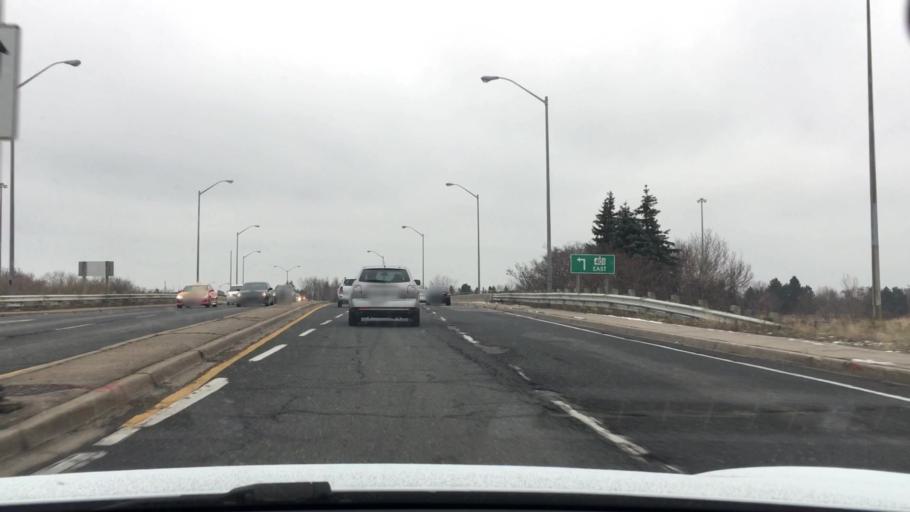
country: CA
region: Ontario
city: Scarborough
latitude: 43.7949
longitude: -79.2163
